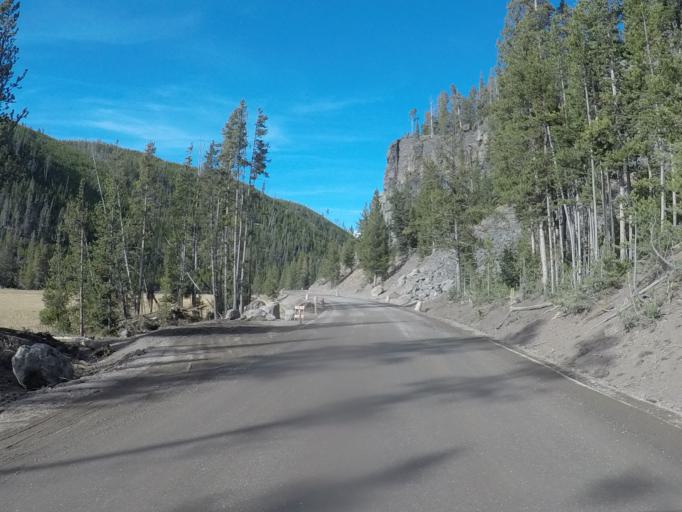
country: US
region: Montana
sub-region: Gallatin County
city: West Yellowstone
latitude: 44.8201
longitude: -110.7278
